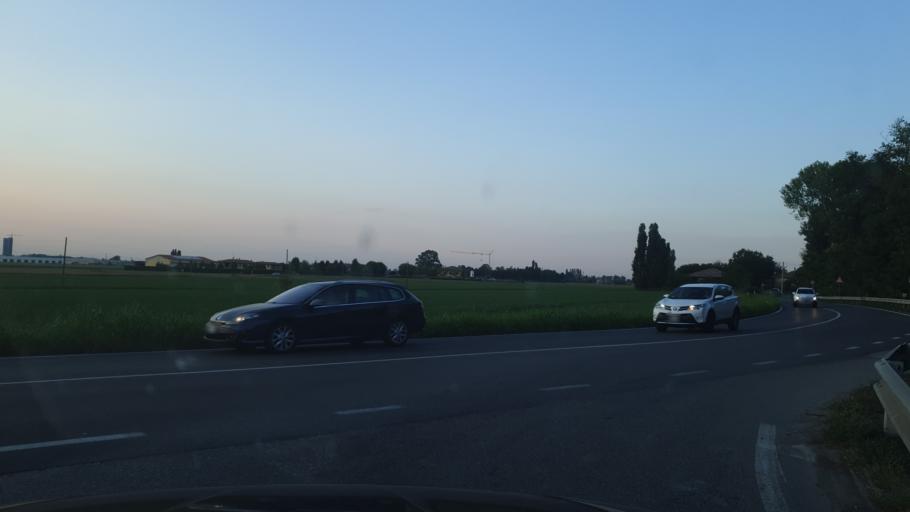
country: IT
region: Emilia-Romagna
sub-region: Provincia di Bologna
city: Progresso
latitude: 44.5515
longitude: 11.3871
